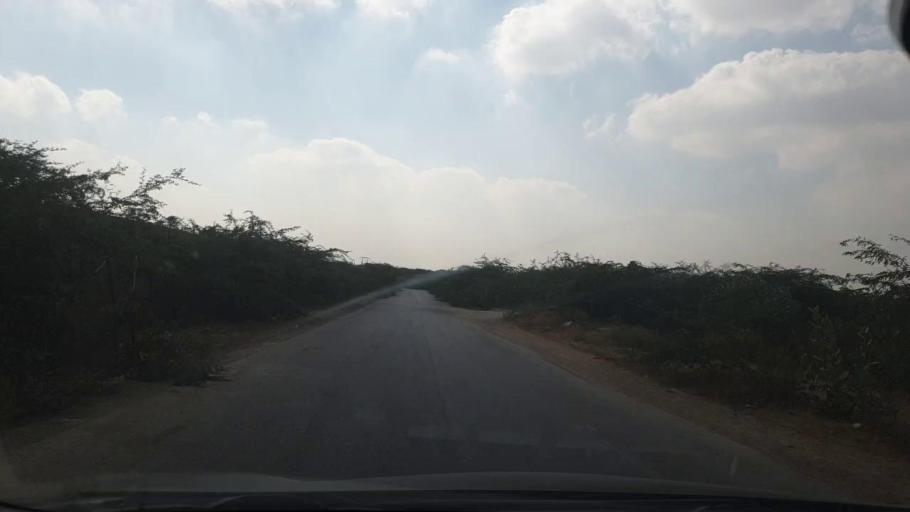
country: PK
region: Sindh
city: Malir Cantonment
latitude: 25.0160
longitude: 67.3530
